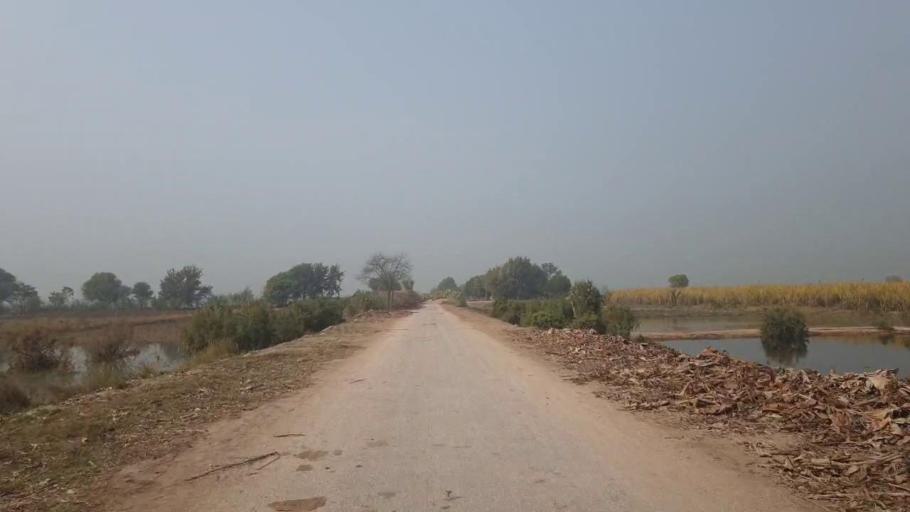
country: PK
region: Sindh
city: Bhit Shah
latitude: 25.8214
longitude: 68.5633
